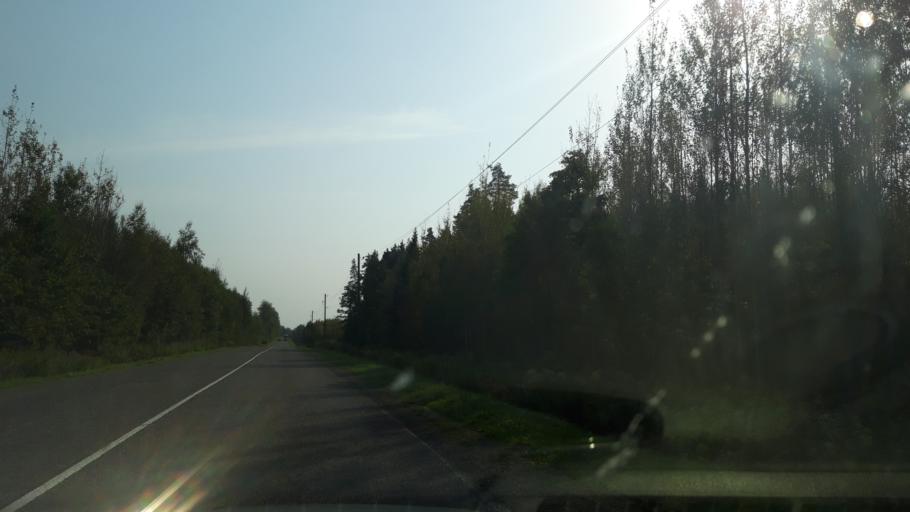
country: LV
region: Burtnieki
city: Matisi
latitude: 57.6376
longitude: 25.2538
